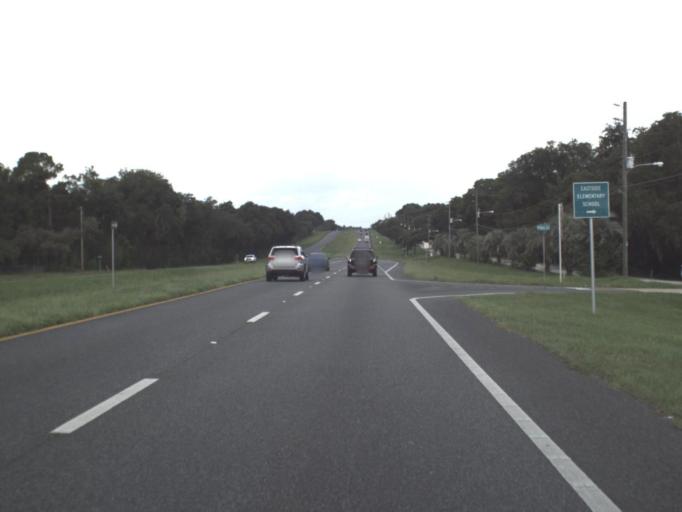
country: US
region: Florida
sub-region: Hernando County
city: Hill 'n Dale
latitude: 28.5234
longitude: -82.2861
